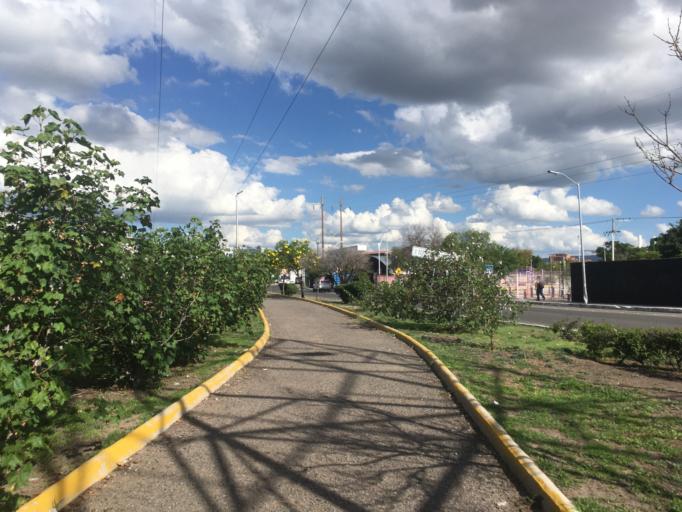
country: MX
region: Queretaro
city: San Jose el Alto
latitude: 20.6227
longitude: -100.3937
